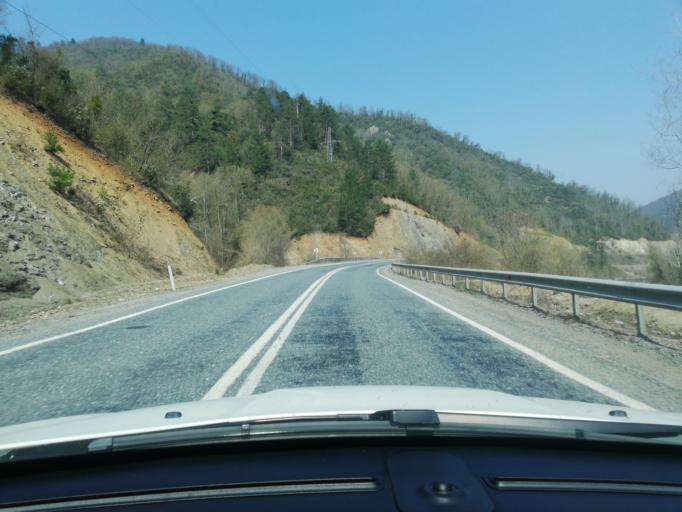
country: TR
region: Zonguldak
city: Gokcebey
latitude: 41.2476
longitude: 32.1683
